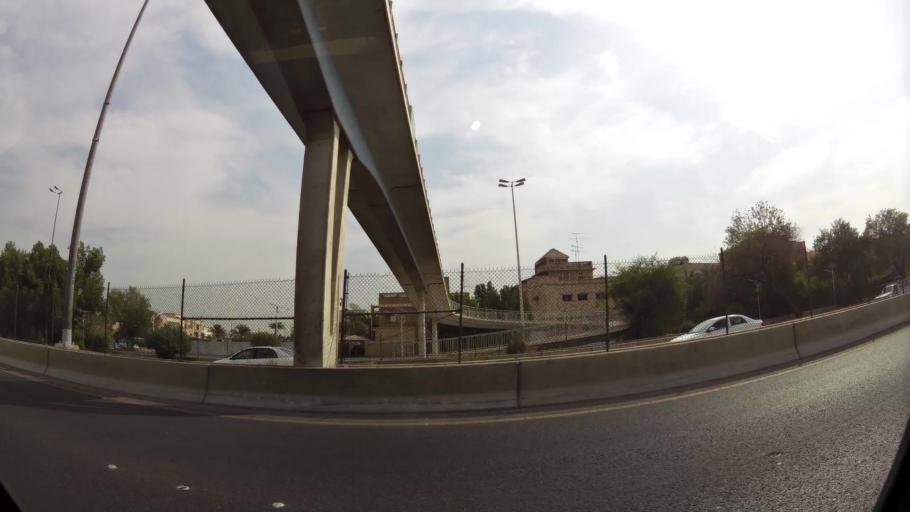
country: KW
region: Al Asimah
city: Ash Shamiyah
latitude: 29.3392
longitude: 47.9719
